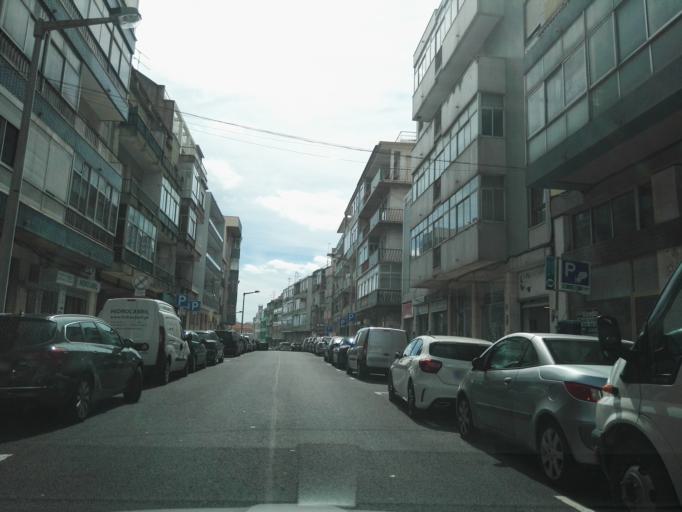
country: PT
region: Lisbon
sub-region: Loures
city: Moscavide
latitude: 38.7591
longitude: -9.1371
